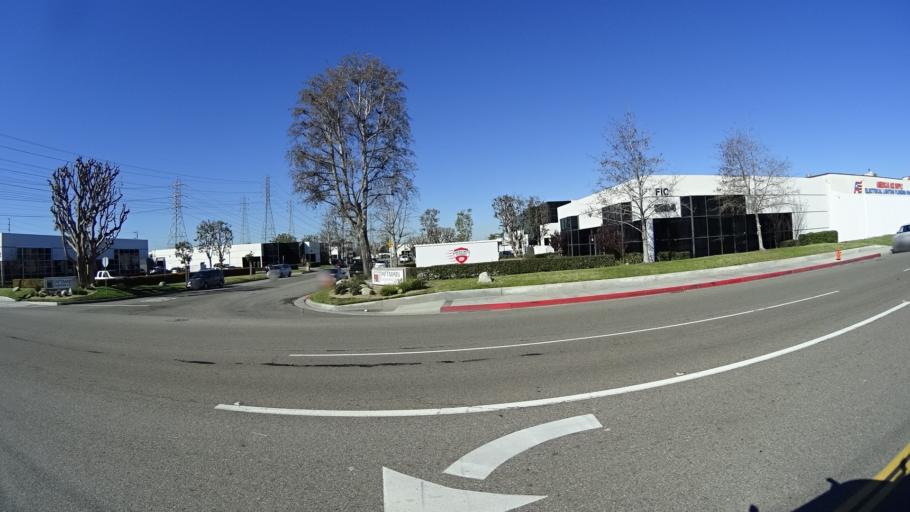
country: US
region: California
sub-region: Orange County
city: Orange
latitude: 33.8137
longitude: -117.8673
